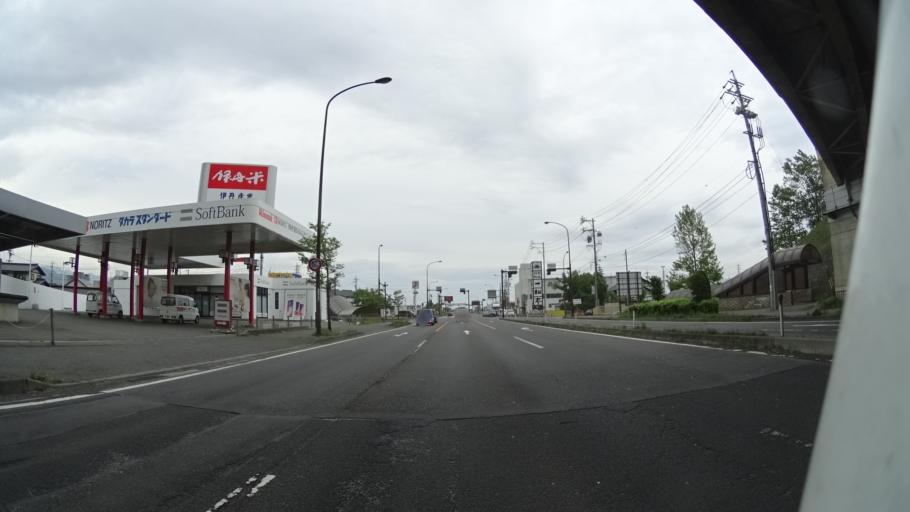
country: JP
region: Nagano
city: Nagano-shi
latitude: 36.5520
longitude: 138.1360
